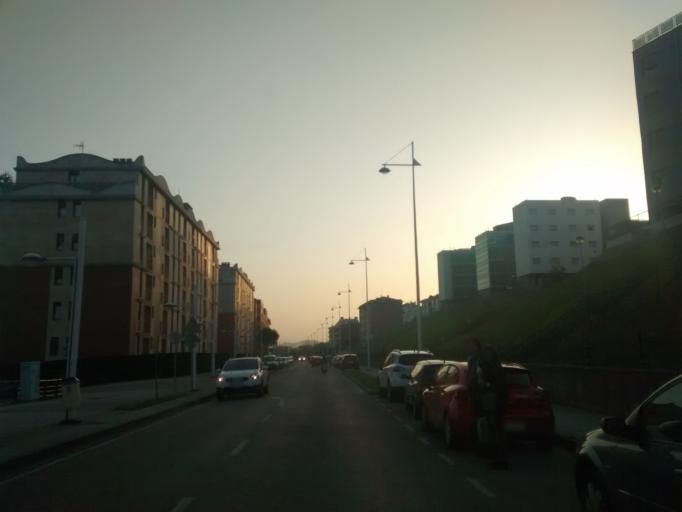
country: ES
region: Cantabria
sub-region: Provincia de Cantabria
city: Santander
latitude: 43.4758
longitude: -3.8040
